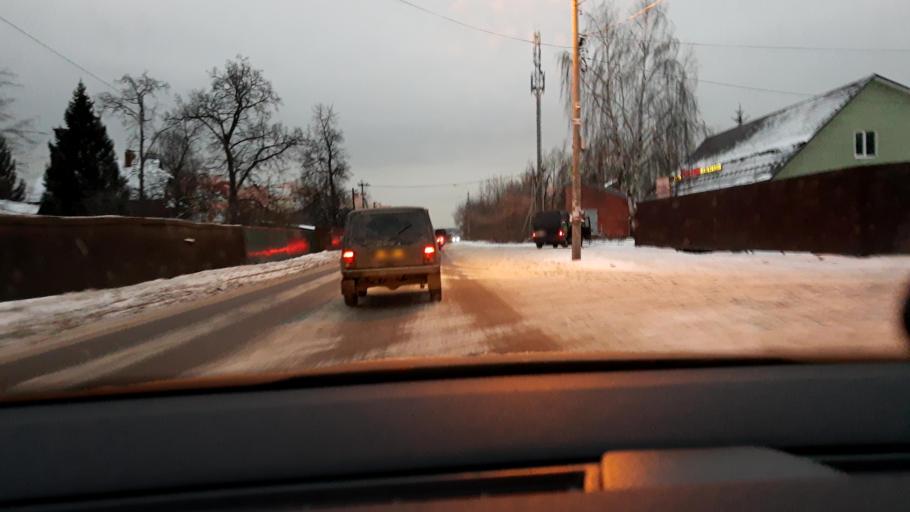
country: RU
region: Moskovskaya
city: Tomilino
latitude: 55.6429
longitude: 37.9478
